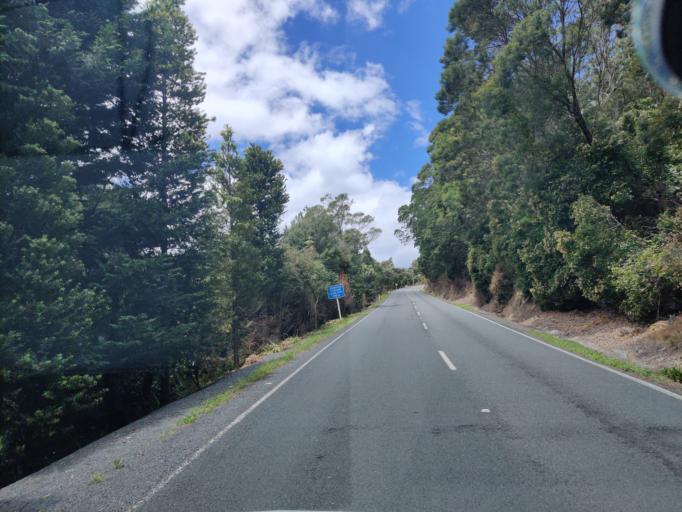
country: NZ
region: Northland
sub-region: Far North District
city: Paihia
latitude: -35.2661
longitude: 174.1304
